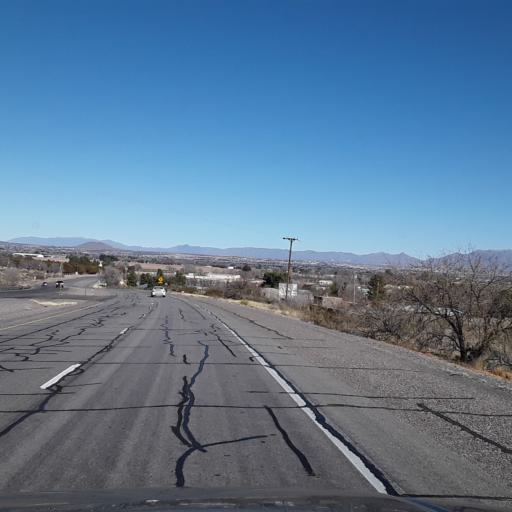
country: US
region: New Mexico
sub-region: Dona Ana County
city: Mesilla
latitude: 32.2957
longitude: -106.8575
